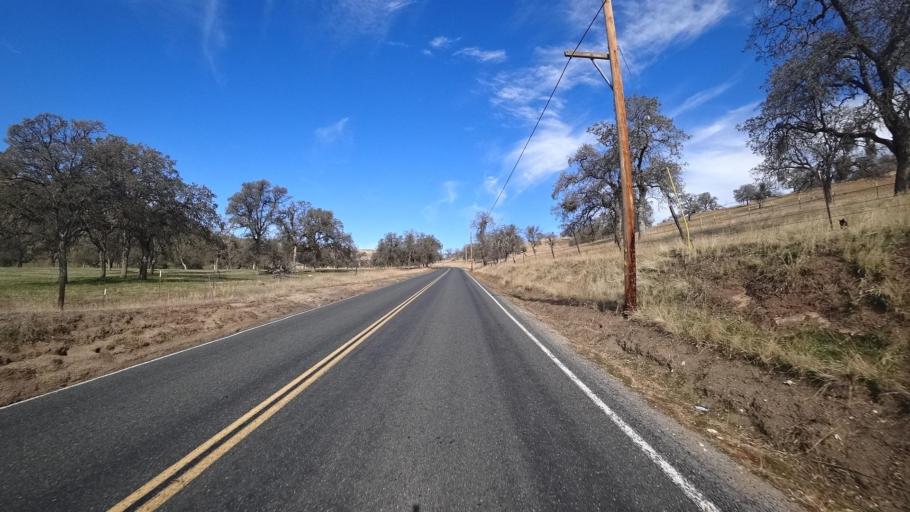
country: US
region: California
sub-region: Kern County
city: Alta Sierra
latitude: 35.6319
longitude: -118.8003
